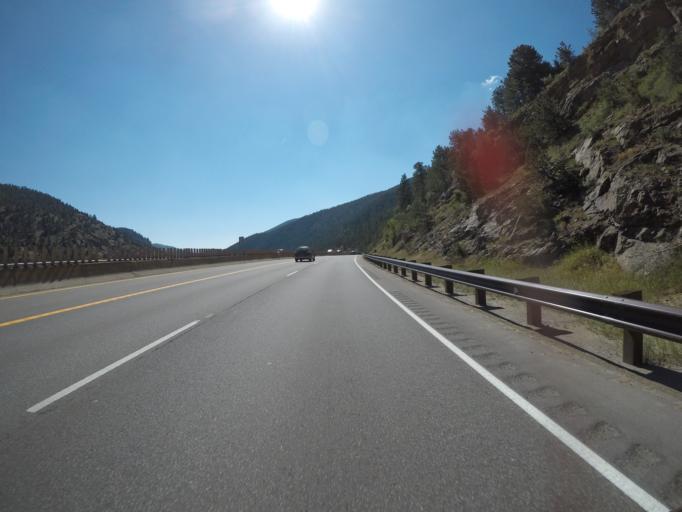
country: US
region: Colorado
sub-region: Clear Creek County
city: Idaho Springs
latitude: 39.7413
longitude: -105.5094
